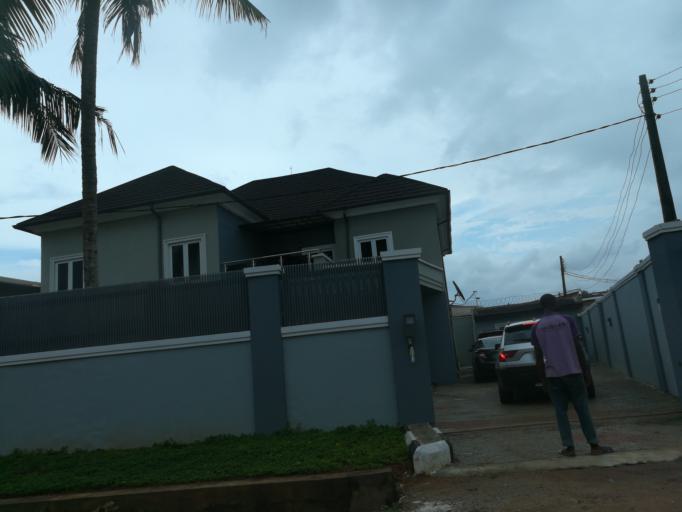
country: NG
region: Lagos
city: Agege
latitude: 6.6015
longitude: 3.3135
